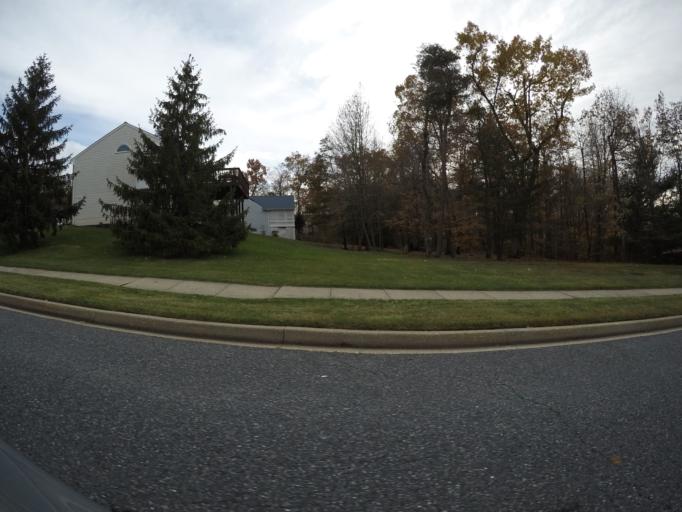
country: US
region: Maryland
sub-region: Harford County
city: Bel Air South
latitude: 39.4703
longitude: -76.2964
